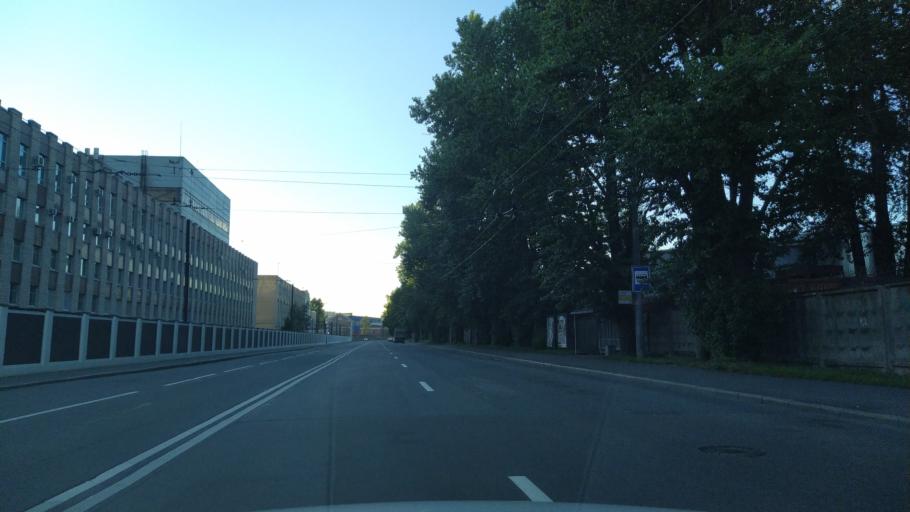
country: RU
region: Leningrad
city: Finlyandskiy
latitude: 59.9572
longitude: 30.3723
